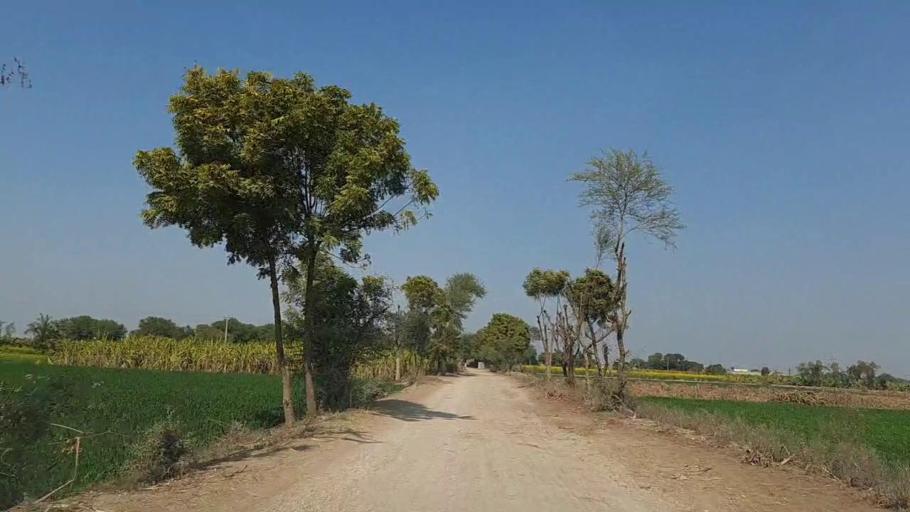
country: PK
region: Sindh
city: Daur
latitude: 26.4979
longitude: 68.2719
